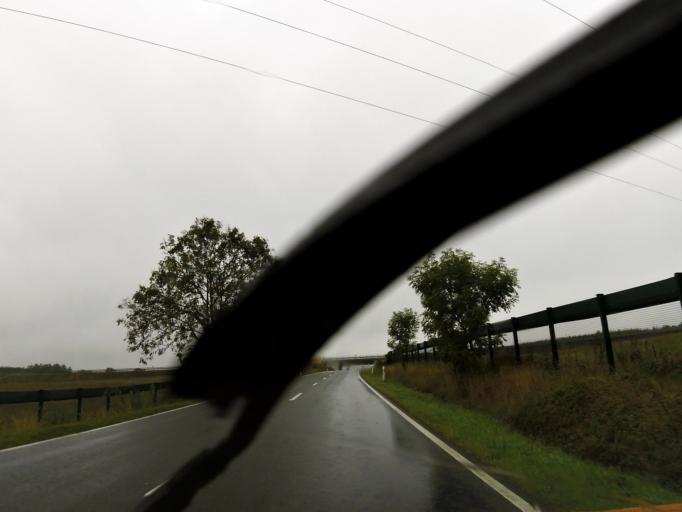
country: DE
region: Lower Saxony
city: Bad Sachsa
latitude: 51.5837
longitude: 10.5159
